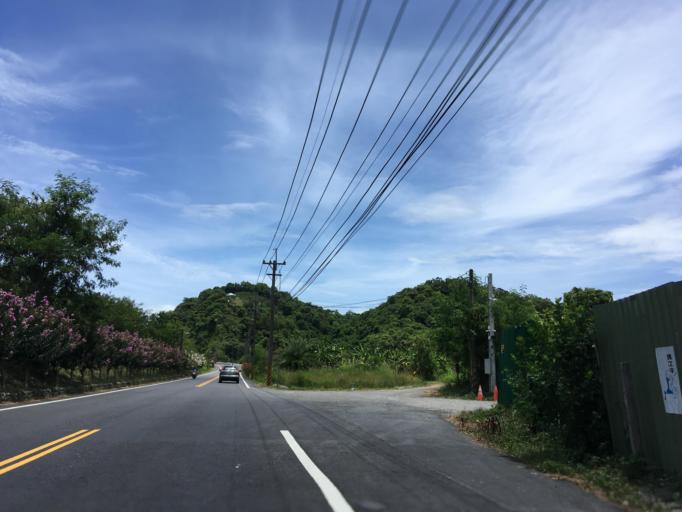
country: TW
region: Taiwan
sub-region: Yilan
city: Yilan
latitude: 24.6419
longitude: 121.7201
